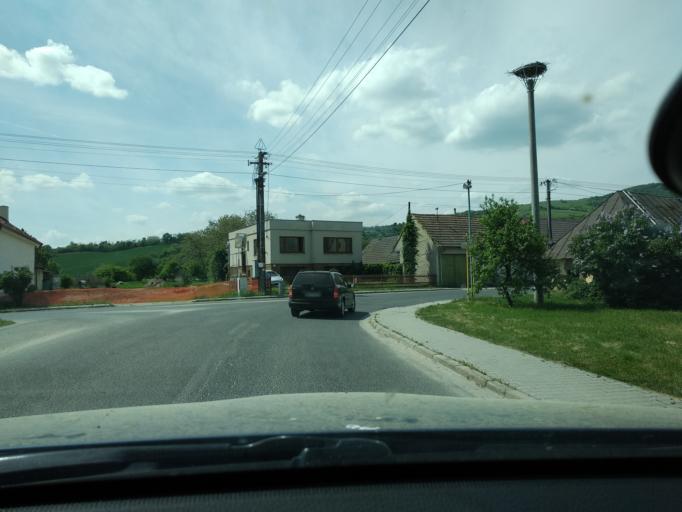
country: SK
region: Trenciansky
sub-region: Okres Nove Mesto nad Vahom
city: Nove Mesto nad Vahom
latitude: 48.8252
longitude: 17.8414
